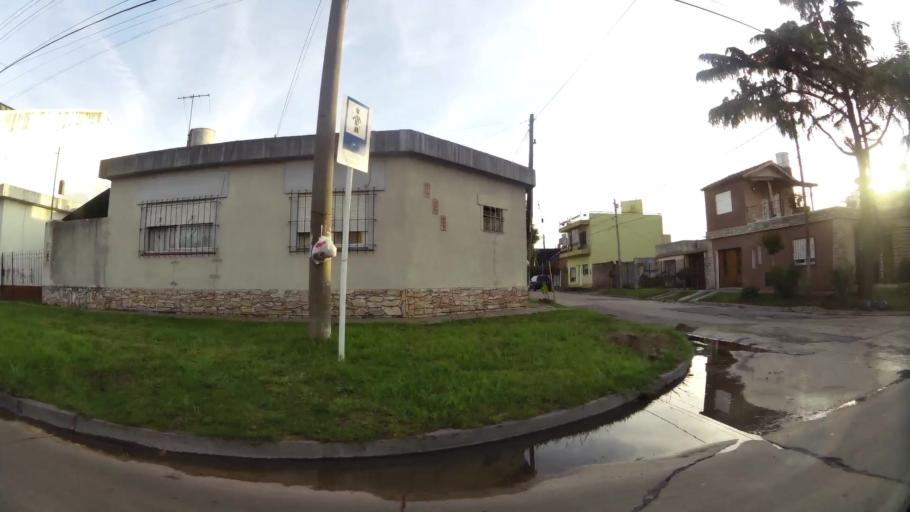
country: AR
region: Buenos Aires
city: Ituzaingo
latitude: -34.6419
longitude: -58.6459
